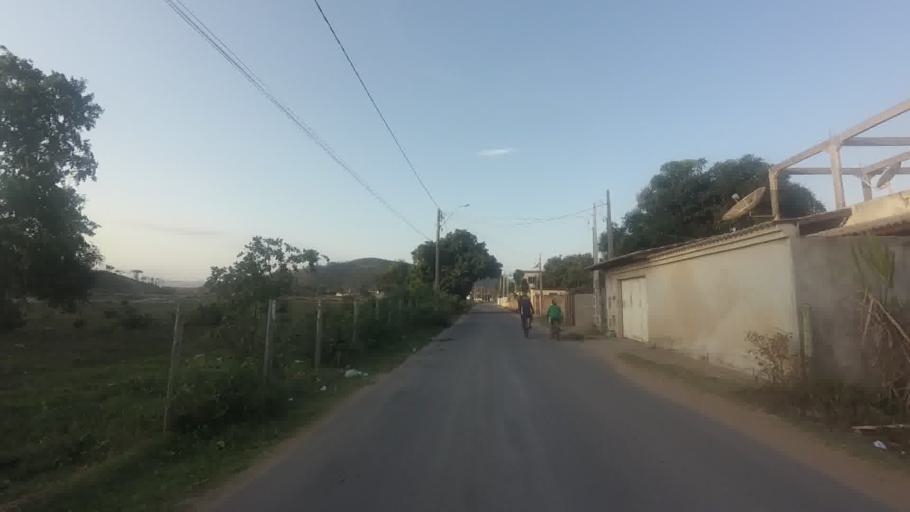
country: BR
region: Espirito Santo
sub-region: Piuma
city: Piuma
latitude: -20.8944
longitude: -40.7844
